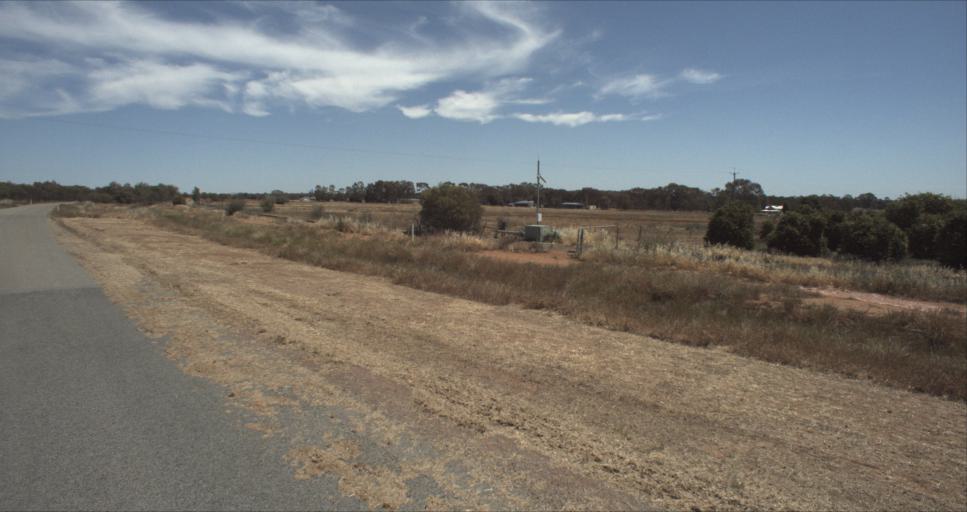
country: AU
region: New South Wales
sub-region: Leeton
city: Leeton
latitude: -34.5794
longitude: 146.4321
